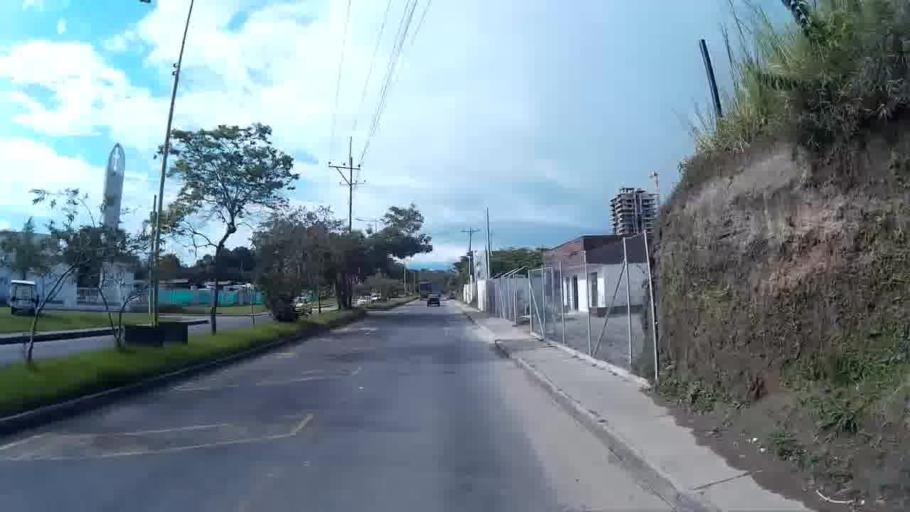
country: CO
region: Quindio
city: Calarca
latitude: 4.5451
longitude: -75.6572
